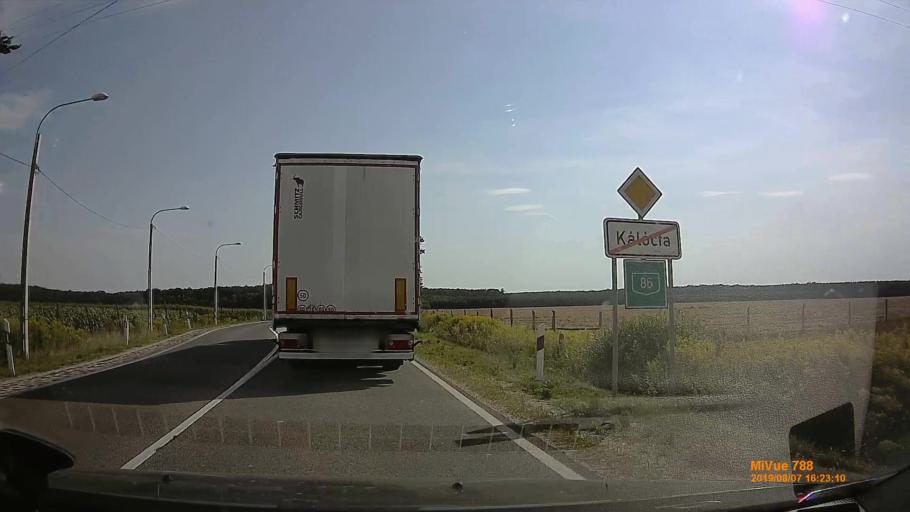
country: HU
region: Zala
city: Zalalovo
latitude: 46.7500
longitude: 16.5580
